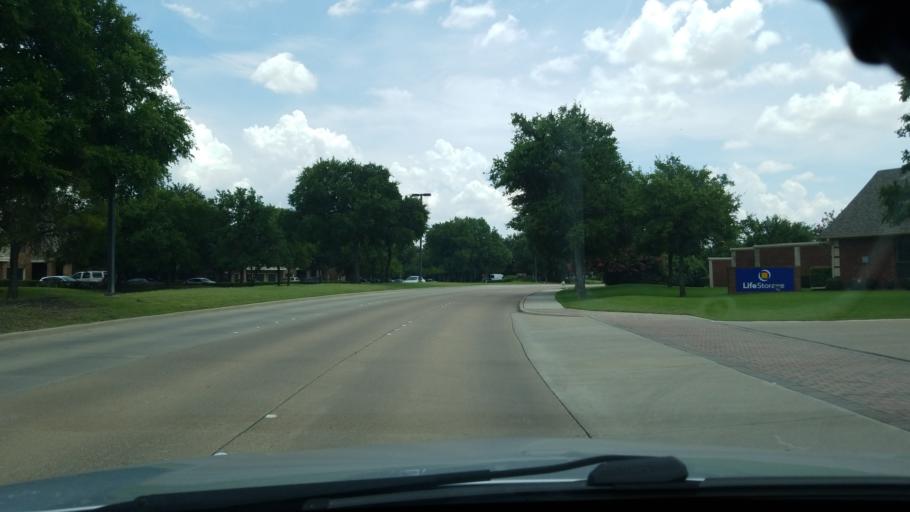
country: US
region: Texas
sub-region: Dallas County
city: Coppell
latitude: 32.9577
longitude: -96.9573
